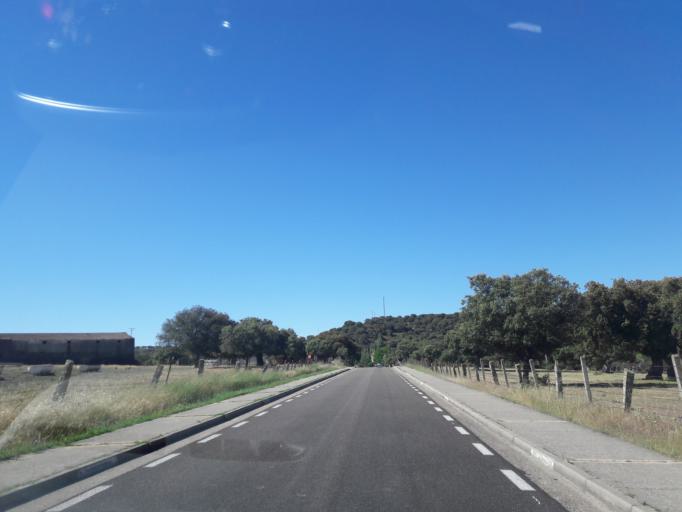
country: ES
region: Castille and Leon
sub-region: Provincia de Salamanca
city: Juzbado
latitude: 41.0746
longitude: -5.8993
